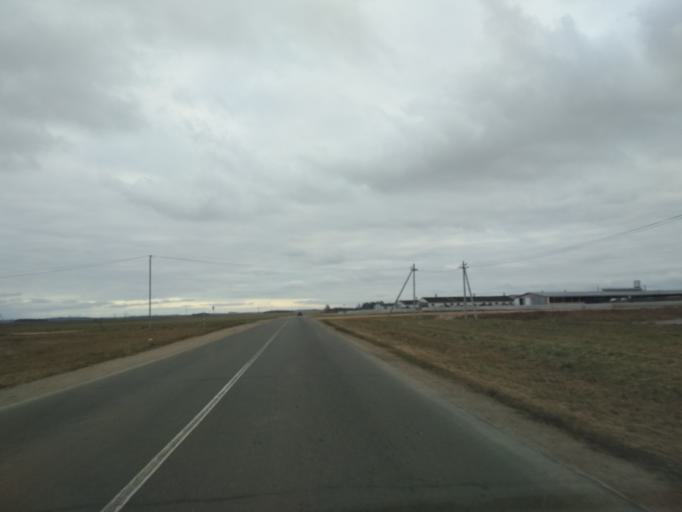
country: BY
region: Minsk
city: Svislach
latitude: 53.5680
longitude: 28.0119
